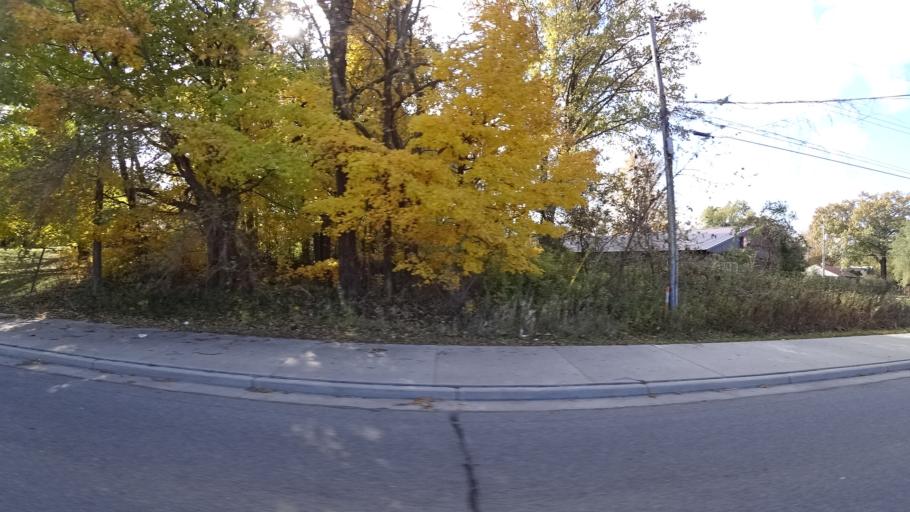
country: US
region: Indiana
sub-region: LaPorte County
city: Trail Creek
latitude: 41.7068
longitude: -86.8623
